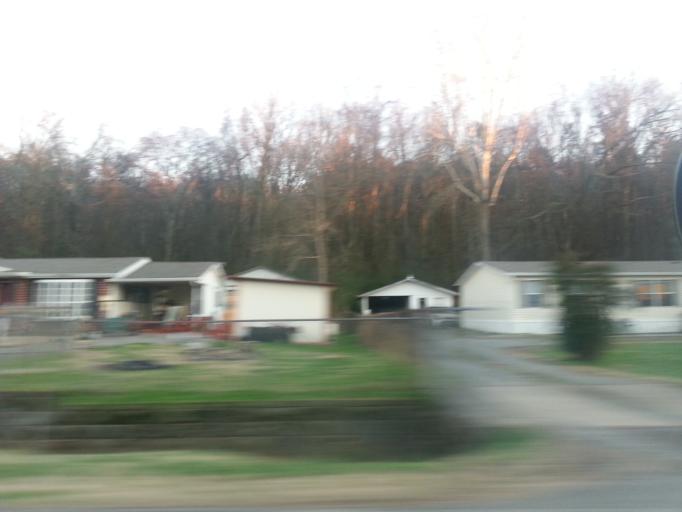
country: US
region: Tennessee
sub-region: Blount County
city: Eagleton Village
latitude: 35.8285
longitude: -83.9394
